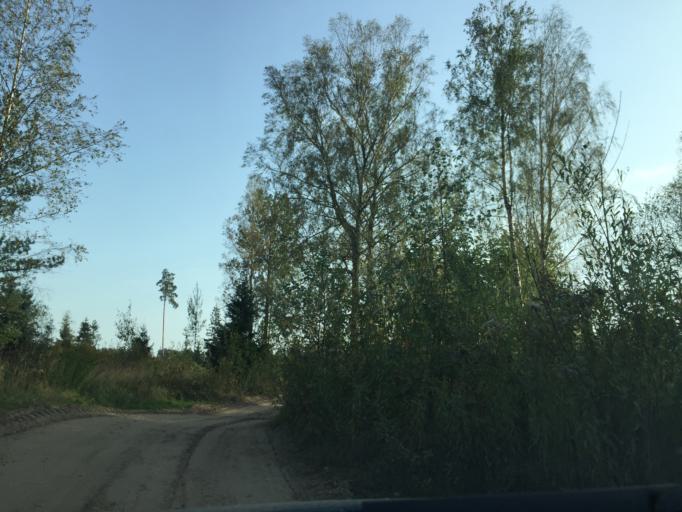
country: LV
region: Garkalne
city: Garkalne
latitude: 56.9711
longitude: 24.4177
